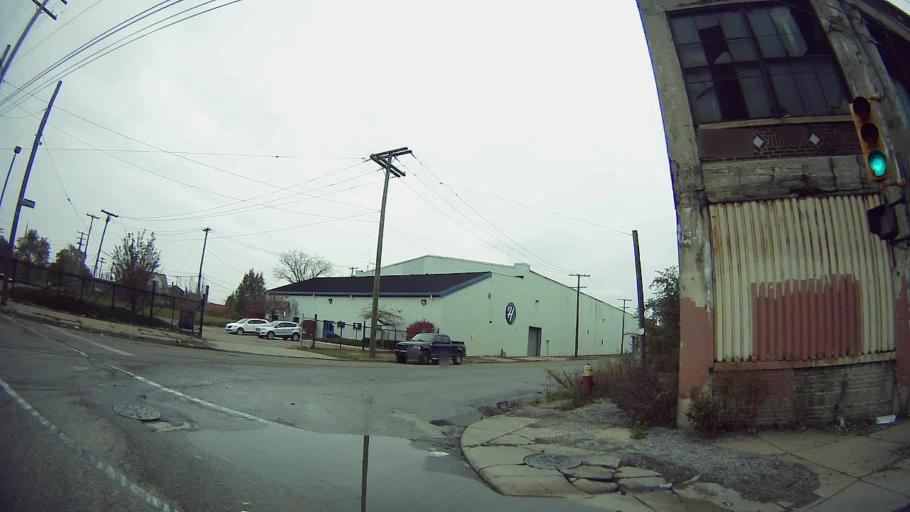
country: US
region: Michigan
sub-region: Wayne County
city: Hamtramck
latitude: 42.3854
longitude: -83.0385
